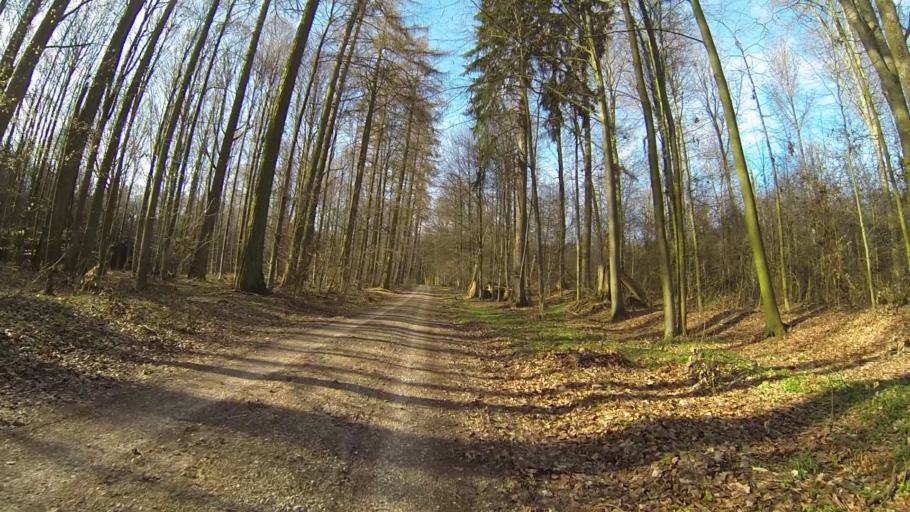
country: DE
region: Baden-Wuerttemberg
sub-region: Regierungsbezirk Stuttgart
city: Niederstotzingen
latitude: 48.5575
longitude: 10.2300
